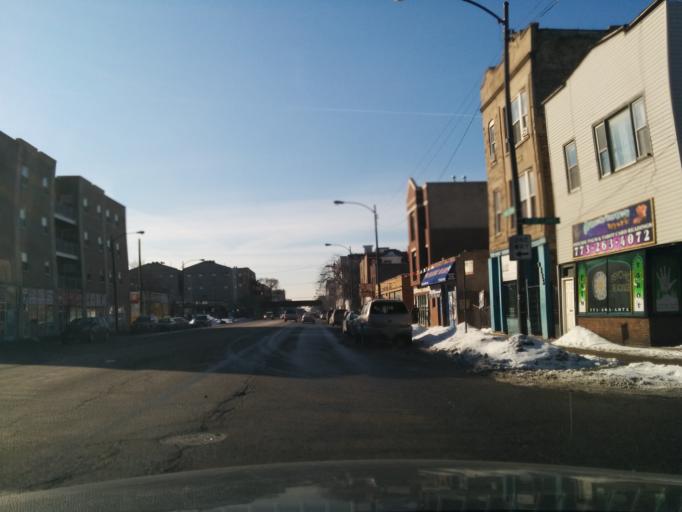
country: US
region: Illinois
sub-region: Cook County
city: Chicago
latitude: 41.9158
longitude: -87.6875
